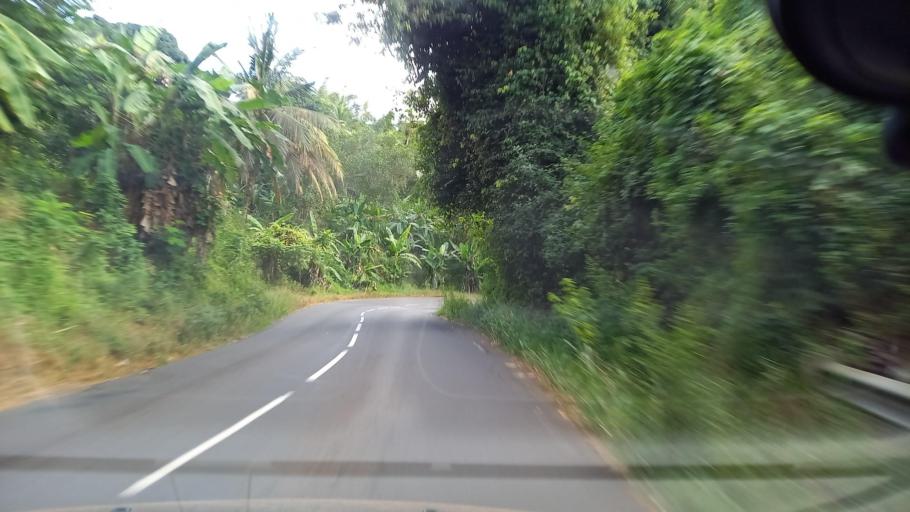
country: YT
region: Dembeni
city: Dembeni
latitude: -12.8398
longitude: 45.1637
